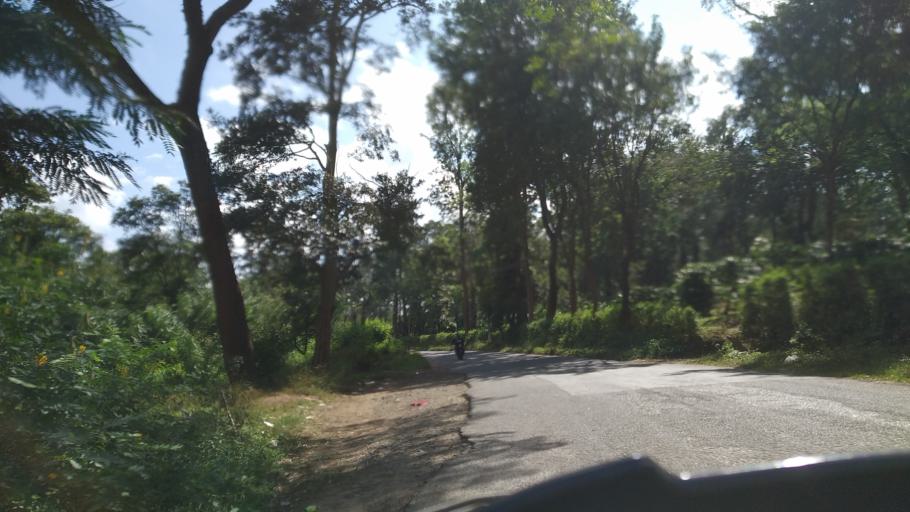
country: IN
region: Karnataka
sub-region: Kodagu
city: Ponnampet
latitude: 11.9565
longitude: 76.0630
